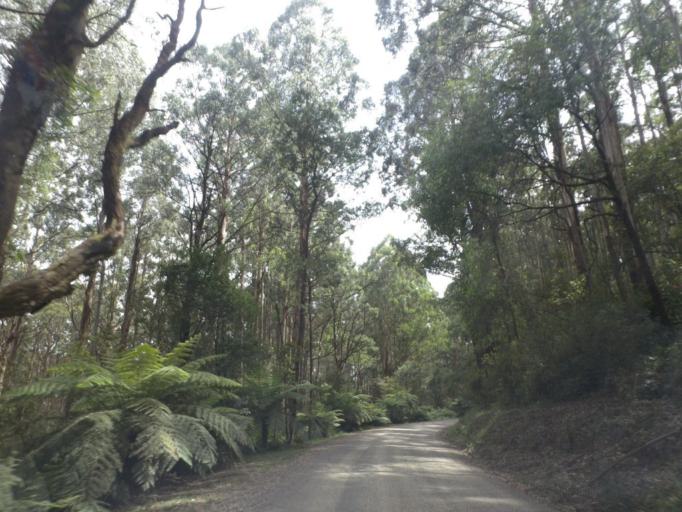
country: AU
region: Victoria
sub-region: Yarra Ranges
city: Healesville
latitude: -37.5131
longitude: 145.5117
